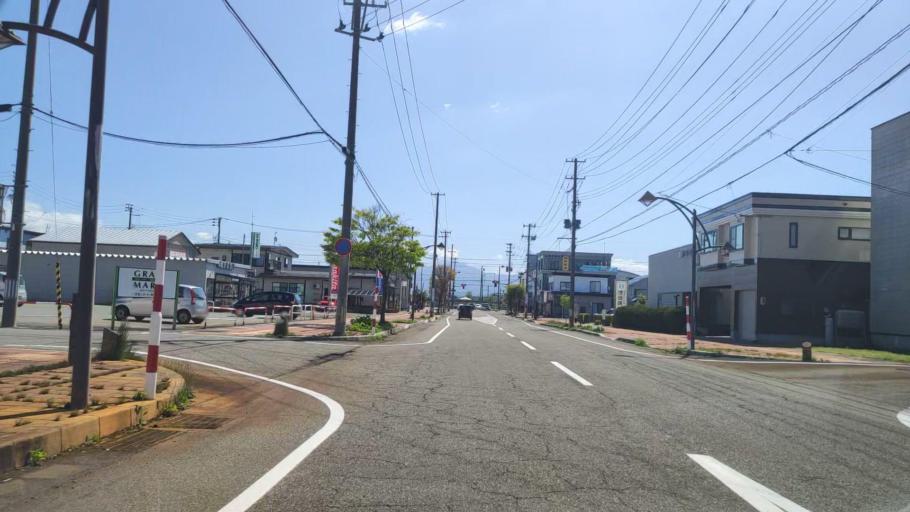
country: JP
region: Akita
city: Omagari
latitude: 39.4620
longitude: 140.4795
